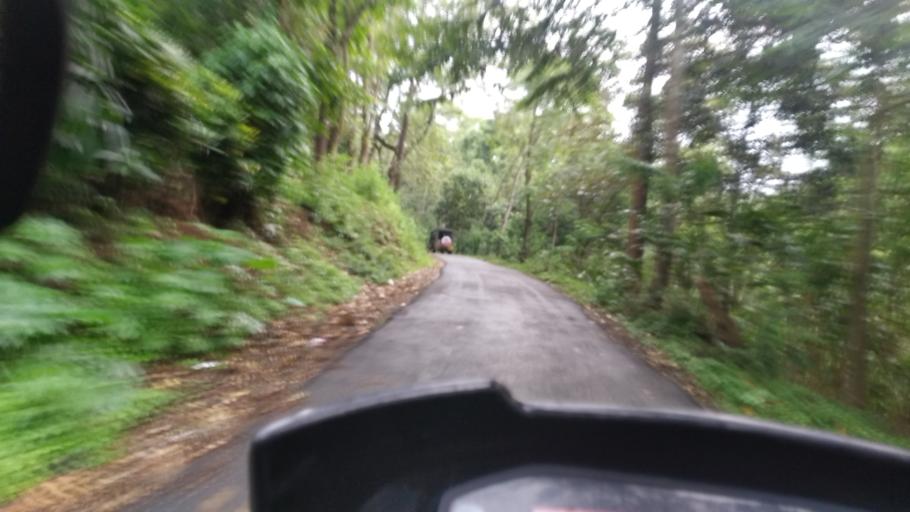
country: IN
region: Tamil Nadu
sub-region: Theni
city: Gudalur
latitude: 9.5543
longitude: 77.0677
